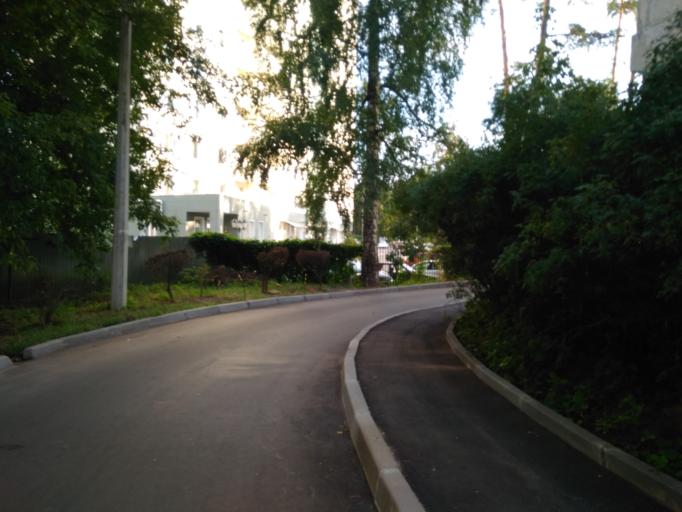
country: RU
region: Moskovskaya
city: Zhukovskiy
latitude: 55.5840
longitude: 38.1374
